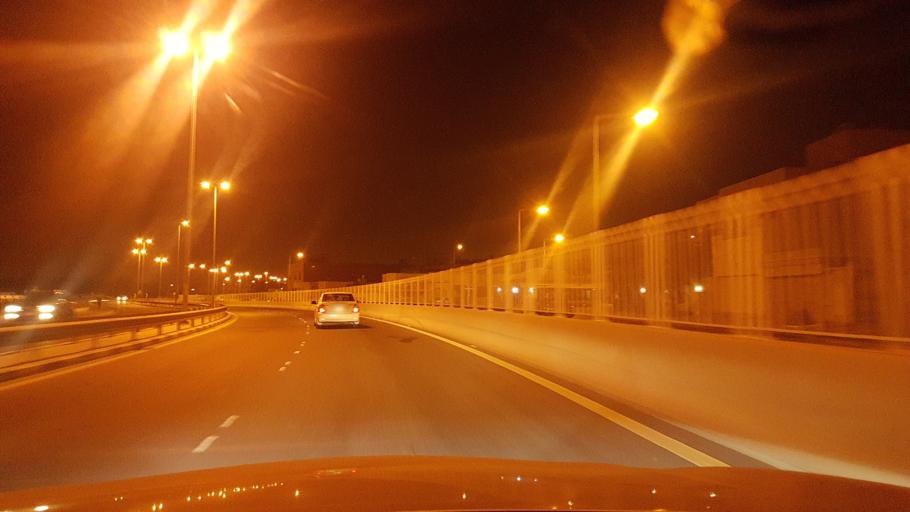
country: BH
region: Central Governorate
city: Dar Kulayb
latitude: 26.0855
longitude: 50.5021
